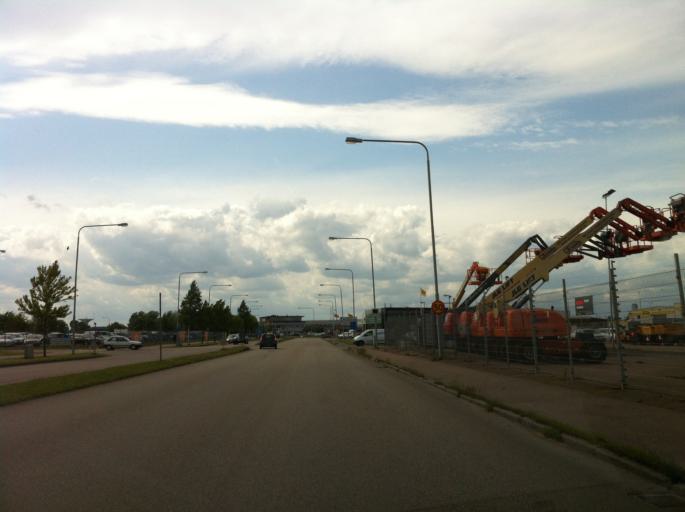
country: SE
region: Skane
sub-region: Landskrona
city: Landskrona
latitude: 55.8672
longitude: 12.8542
